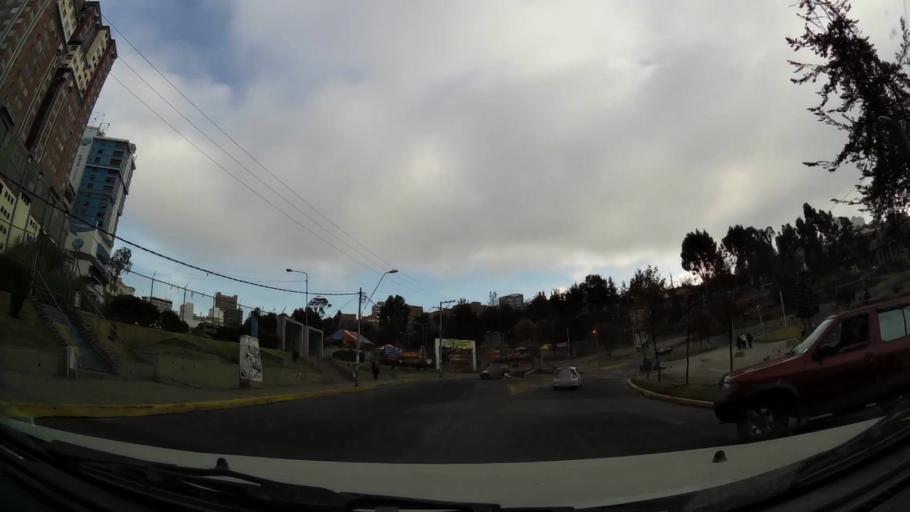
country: BO
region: La Paz
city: La Paz
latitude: -16.5027
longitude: -68.1288
